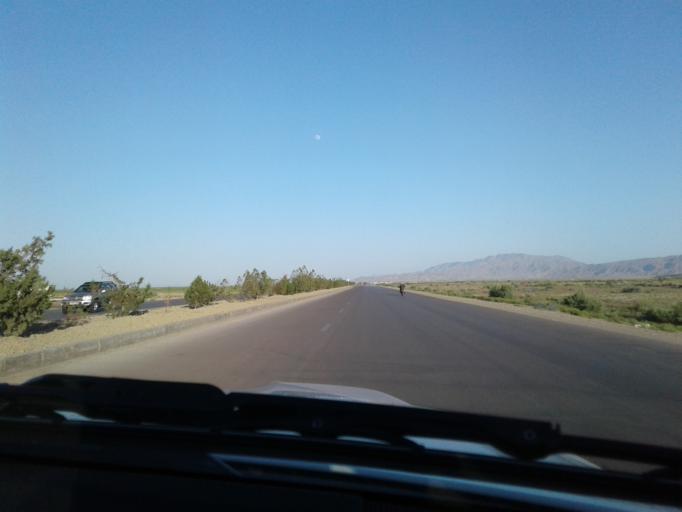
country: TM
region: Ahal
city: Baharly
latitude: 38.3639
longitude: 57.5272
